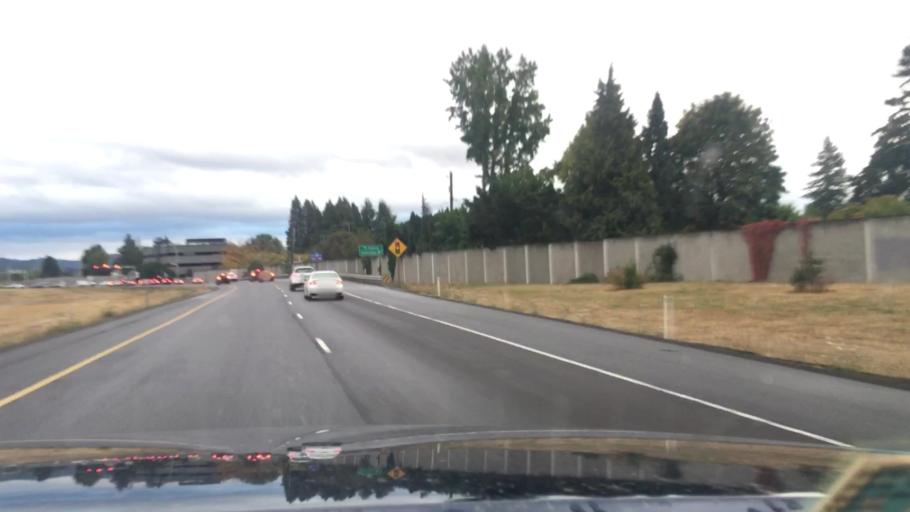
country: US
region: Oregon
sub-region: Lane County
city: Eugene
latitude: 44.0873
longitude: -123.0716
